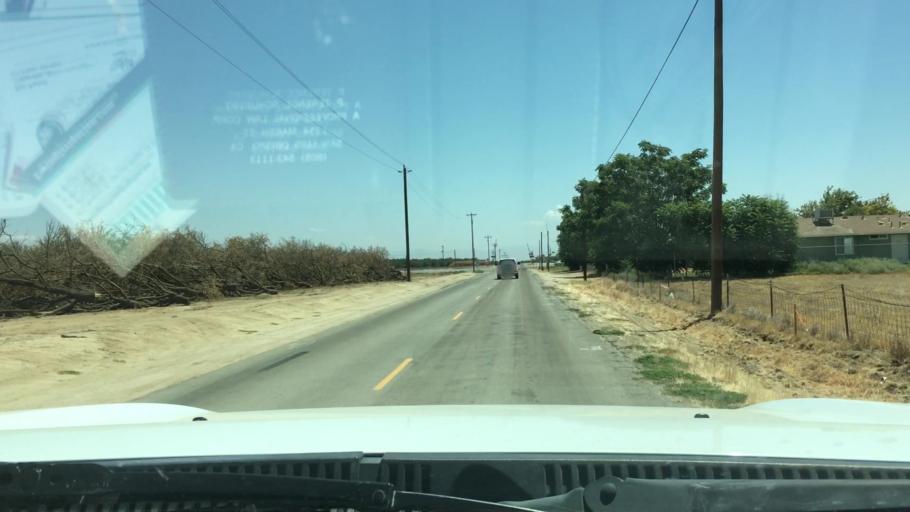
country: US
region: California
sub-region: Kern County
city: Shafter
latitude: 35.5290
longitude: -119.3089
